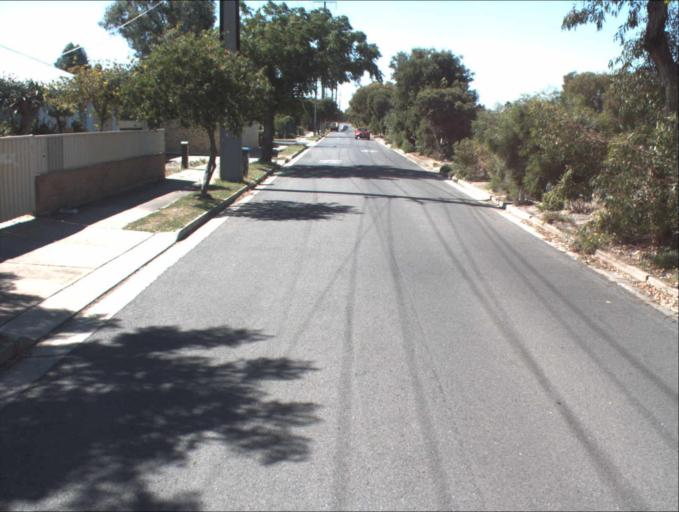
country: AU
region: South Australia
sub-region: Port Adelaide Enfield
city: Birkenhead
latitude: -34.8035
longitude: 138.4989
